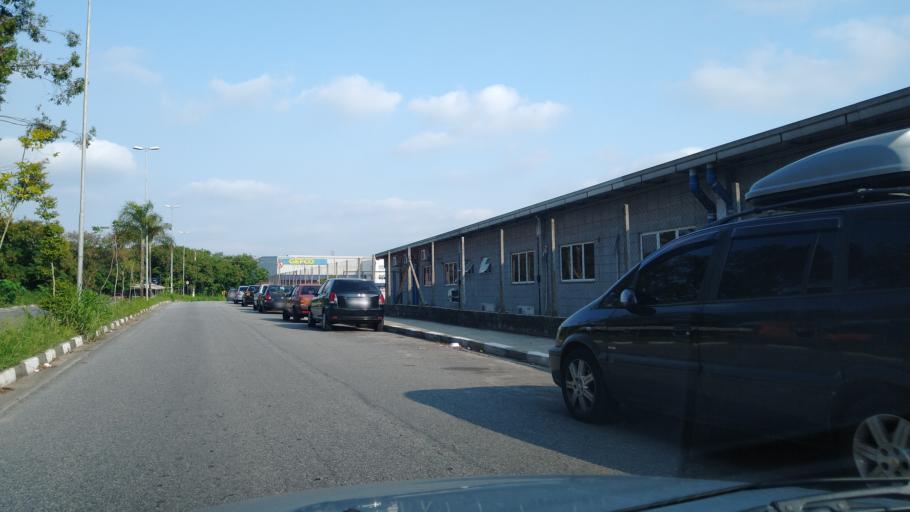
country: BR
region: Sao Paulo
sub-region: Guarulhos
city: Guarulhos
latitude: -23.4894
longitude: -46.5406
